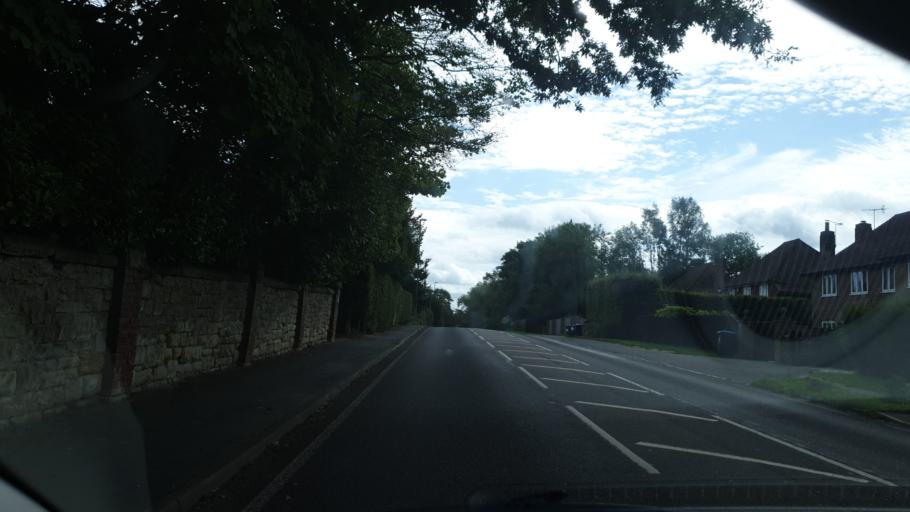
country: GB
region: England
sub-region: West Sussex
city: East Grinstead
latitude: 51.1157
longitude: 0.0150
